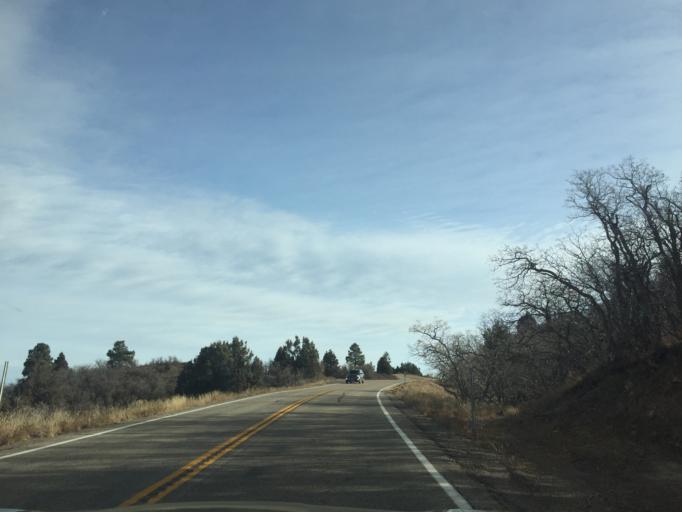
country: US
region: Utah
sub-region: Garfield County
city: Panguitch
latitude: 37.4966
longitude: -112.5376
